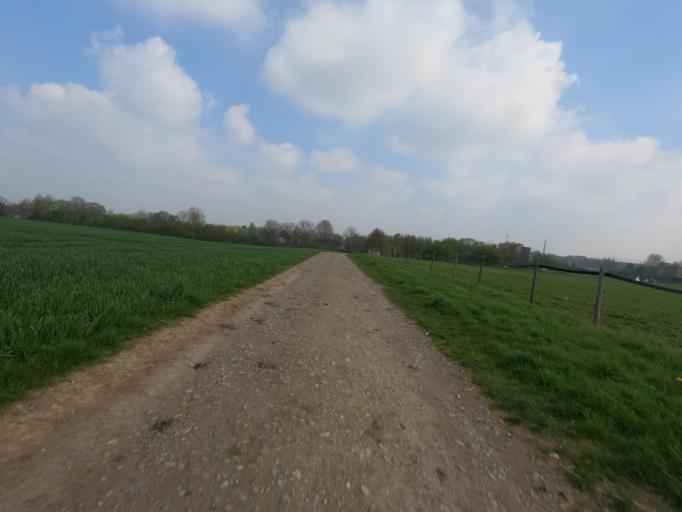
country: DE
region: North Rhine-Westphalia
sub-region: Regierungsbezirk Koln
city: Heinsberg
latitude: 51.0524
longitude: 6.1213
